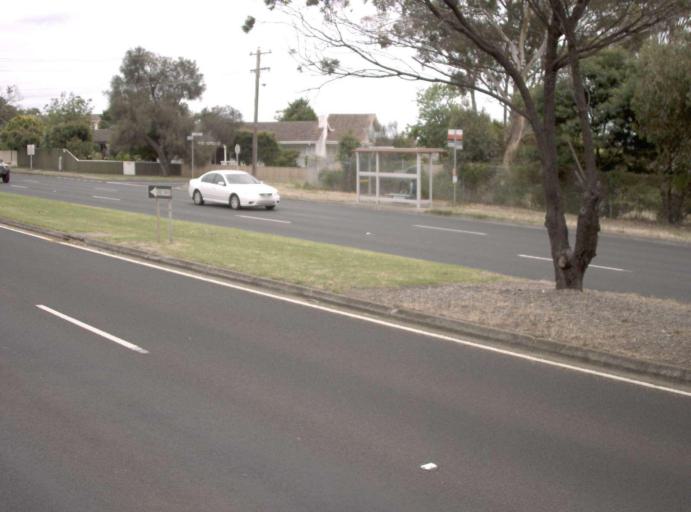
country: AU
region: Victoria
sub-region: Mornington Peninsula
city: Mornington
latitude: -38.2345
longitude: 145.0386
